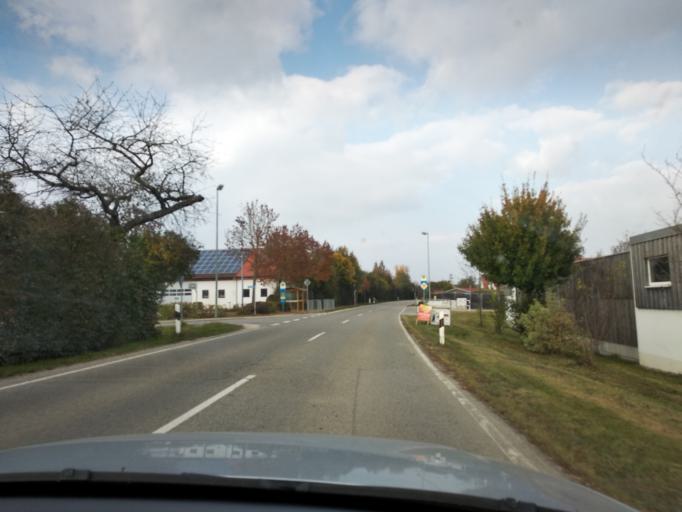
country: DE
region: Bavaria
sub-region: Upper Bavaria
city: Ottenhofen
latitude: 48.2106
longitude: 11.8769
